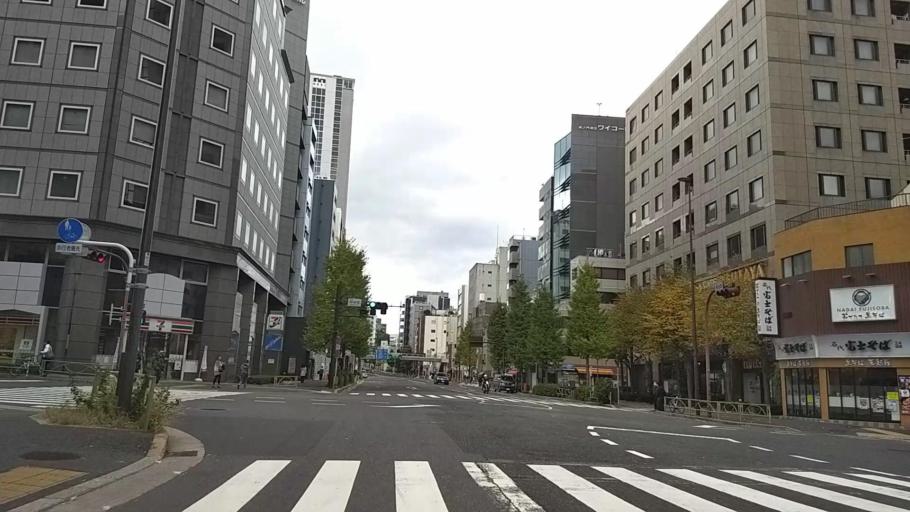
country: JP
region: Tokyo
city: Tokyo
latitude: 35.6633
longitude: 139.7453
